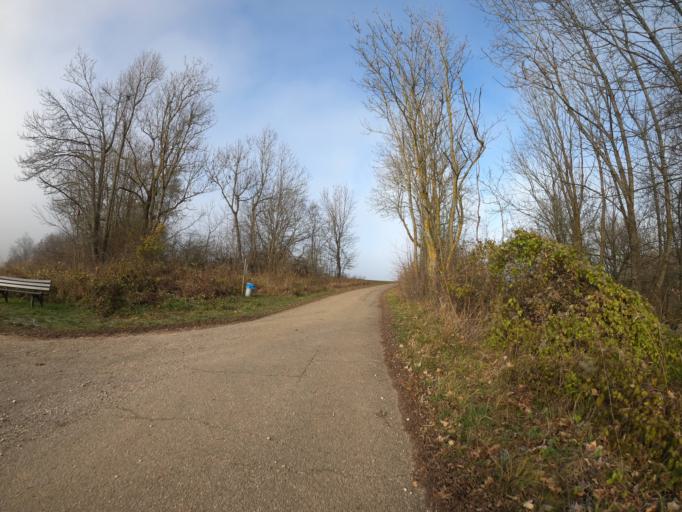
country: DE
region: Baden-Wuerttemberg
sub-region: Regierungsbezirk Stuttgart
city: Deggingen
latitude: 48.5891
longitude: 9.7555
